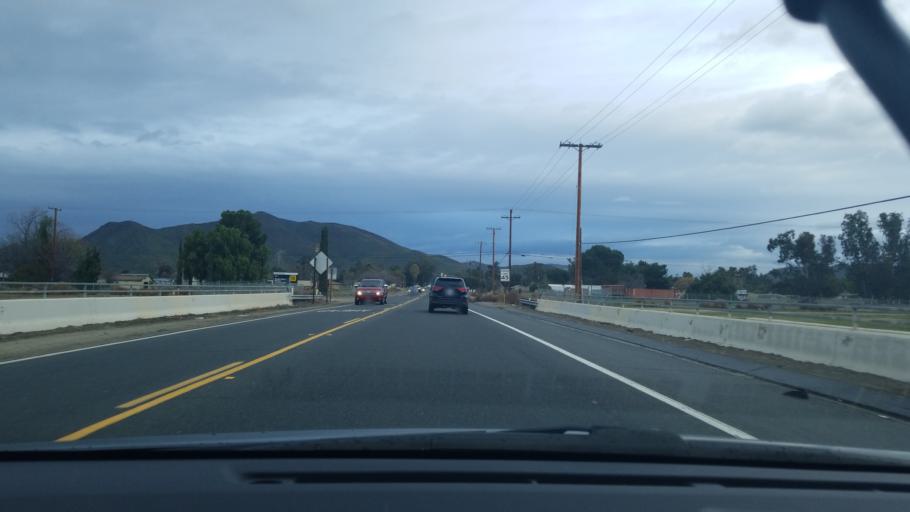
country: US
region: California
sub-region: Riverside County
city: Winchester
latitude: 33.6989
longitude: -117.0848
